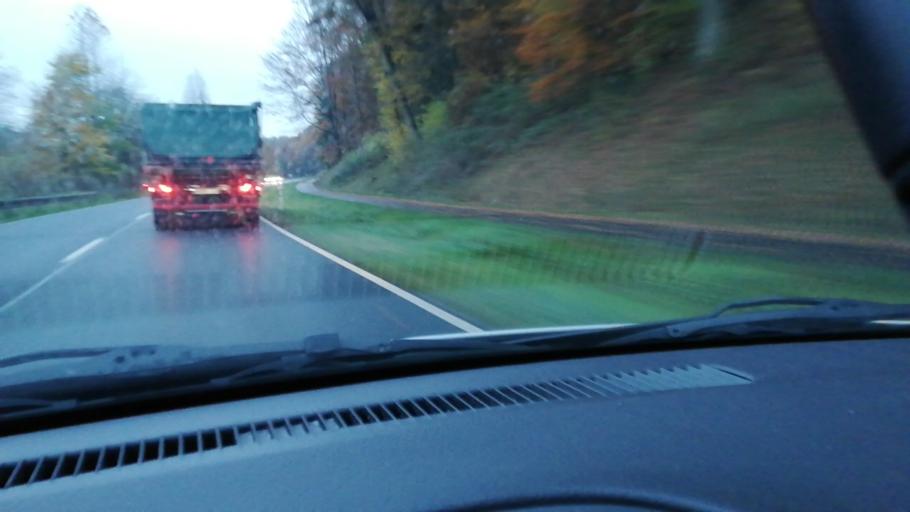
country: DE
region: Bavaria
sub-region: Regierungsbezirk Unterfranken
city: Mombris
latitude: 50.0473
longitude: 9.1958
